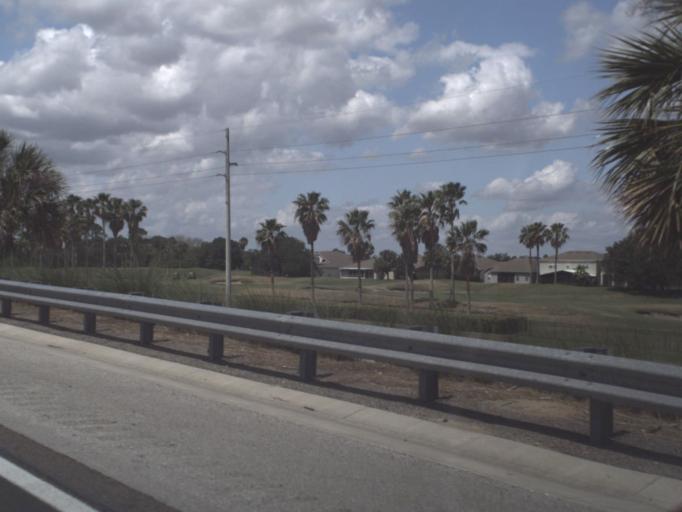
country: US
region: Florida
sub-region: Orange County
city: Oakland
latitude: 28.5134
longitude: -81.6032
